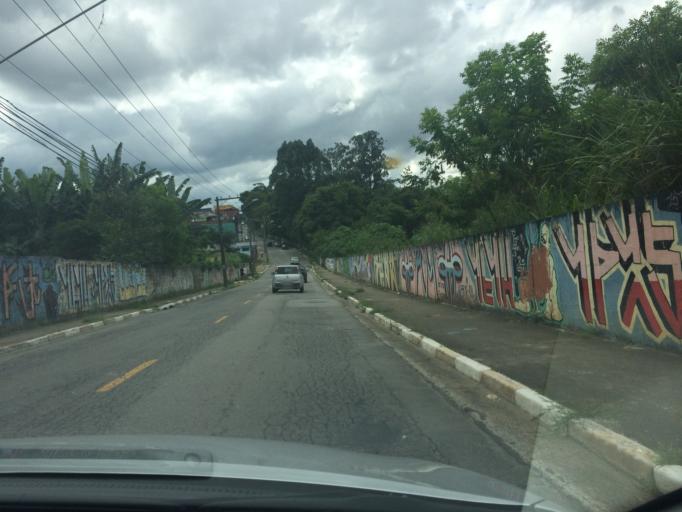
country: BR
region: Sao Paulo
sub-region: Guarulhos
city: Guarulhos
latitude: -23.4331
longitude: -46.5306
